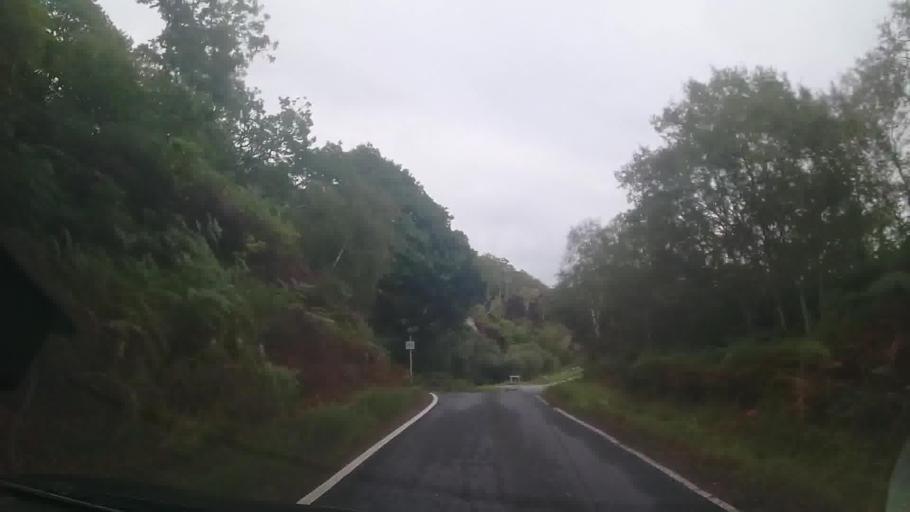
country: GB
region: Scotland
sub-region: Argyll and Bute
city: Isle Of Mull
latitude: 56.6775
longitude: -5.9191
